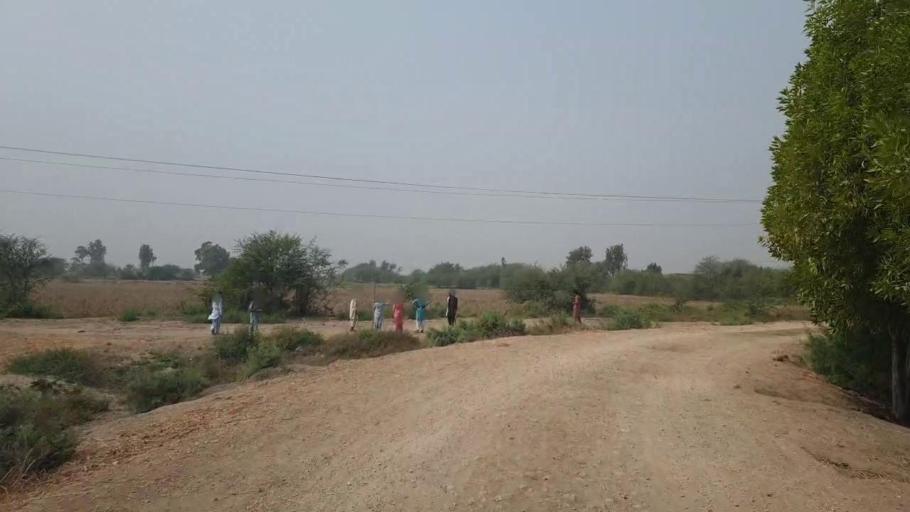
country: PK
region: Sindh
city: Kario
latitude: 24.6576
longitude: 68.6392
